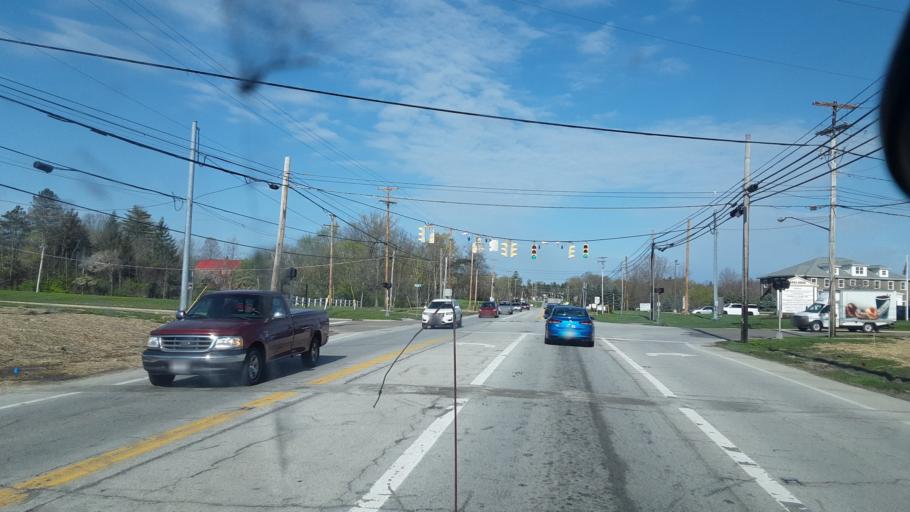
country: US
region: Ohio
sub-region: Medina County
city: Medina
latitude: 41.1382
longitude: -81.8309
